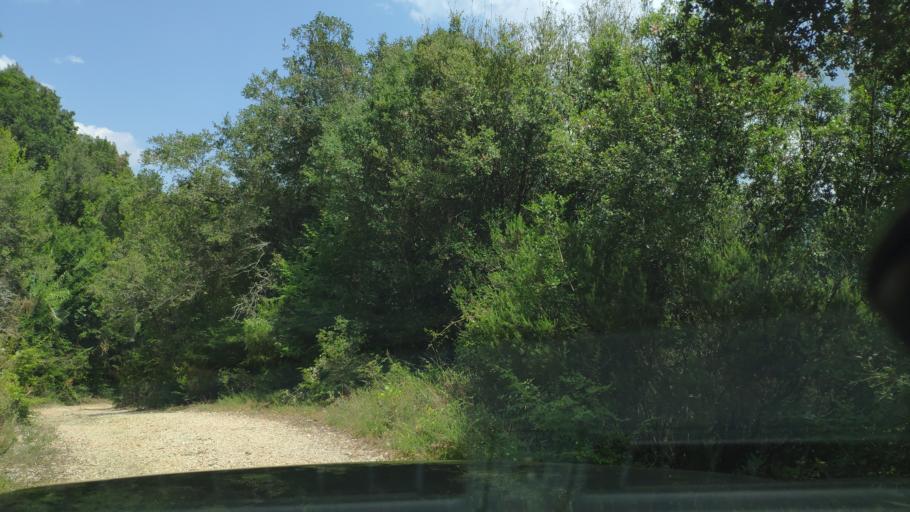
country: GR
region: Epirus
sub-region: Nomos Artas
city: Agios Dimitrios
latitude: 39.3091
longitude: 21.0226
